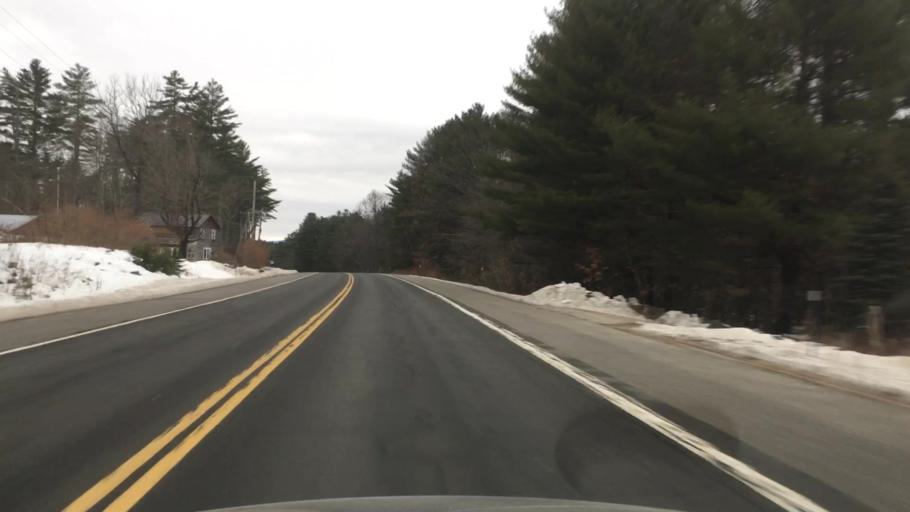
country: US
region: New Hampshire
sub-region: Merrimack County
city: Henniker
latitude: 43.2243
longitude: -71.8849
